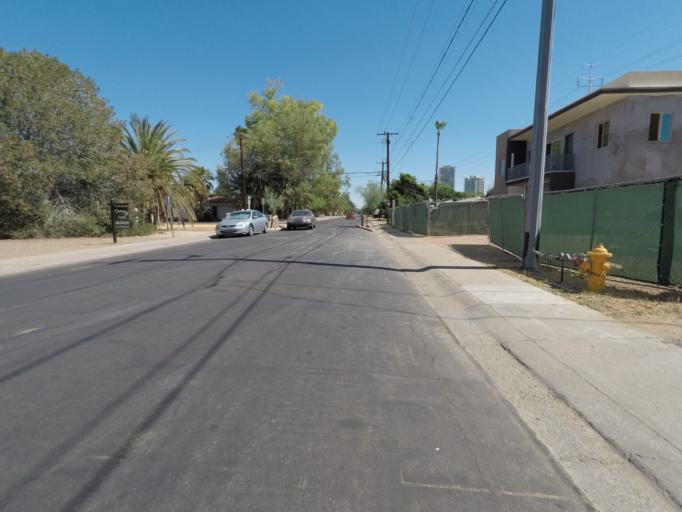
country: US
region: Arizona
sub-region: Maricopa County
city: Tempe Junction
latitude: 33.4174
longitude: -111.9442
